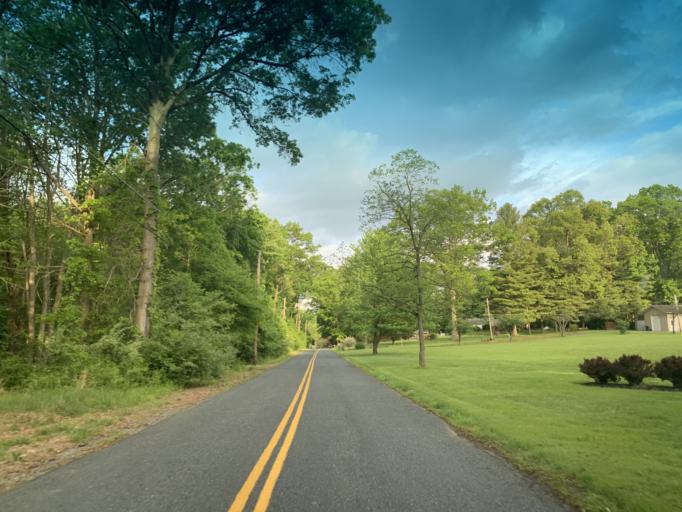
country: US
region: Pennsylvania
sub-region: York County
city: Susquehanna Trails
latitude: 39.6763
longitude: -76.2426
